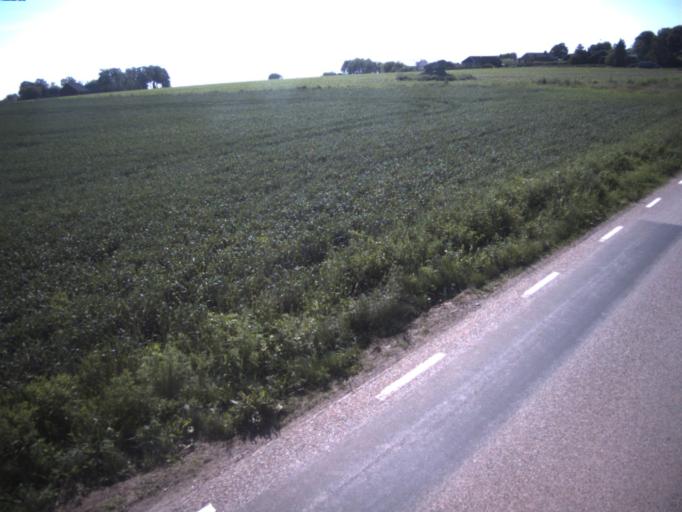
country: SE
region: Skane
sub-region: Helsingborg
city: Gantofta
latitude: 55.9841
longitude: 12.8089
